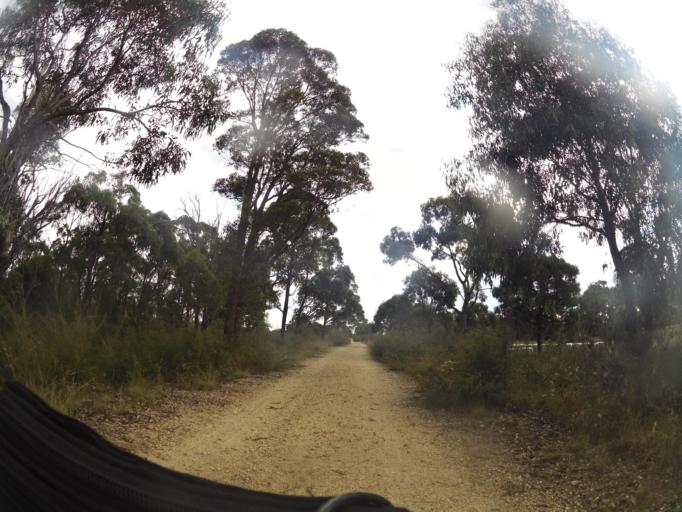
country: AU
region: Victoria
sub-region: Wellington
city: Heyfield
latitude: -38.0443
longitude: 146.6406
